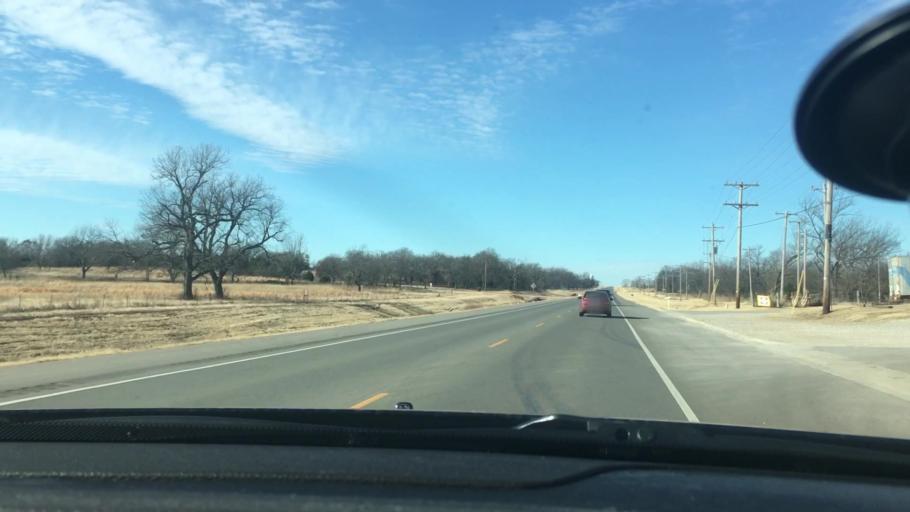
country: US
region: Oklahoma
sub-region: Cleveland County
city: Lexington
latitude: 35.0149
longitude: -97.2492
